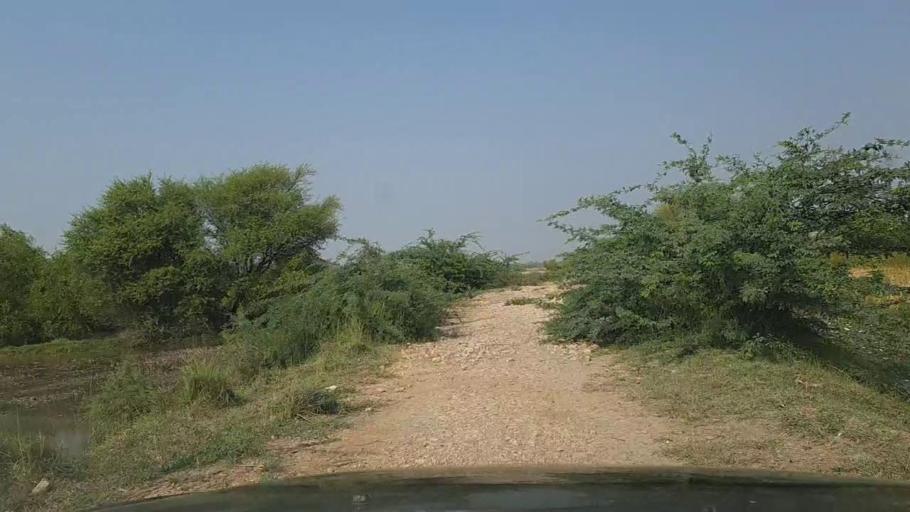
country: PK
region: Sindh
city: Mirpur Batoro
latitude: 24.6861
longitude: 68.2362
